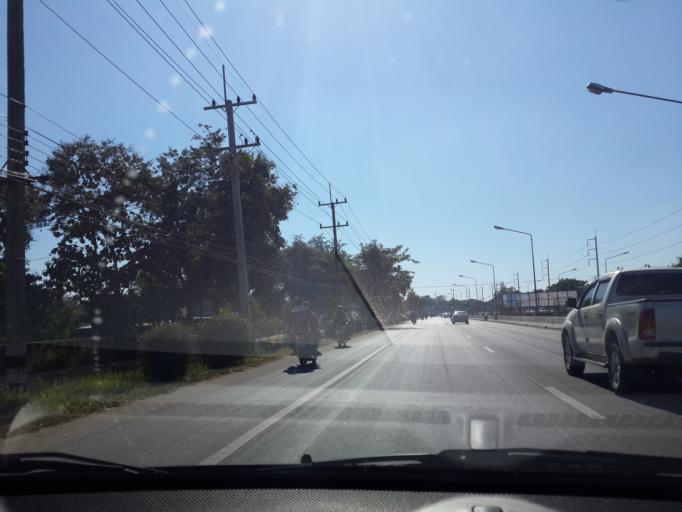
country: TH
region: Chiang Mai
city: Chiang Mai
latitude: 18.7662
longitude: 98.9479
